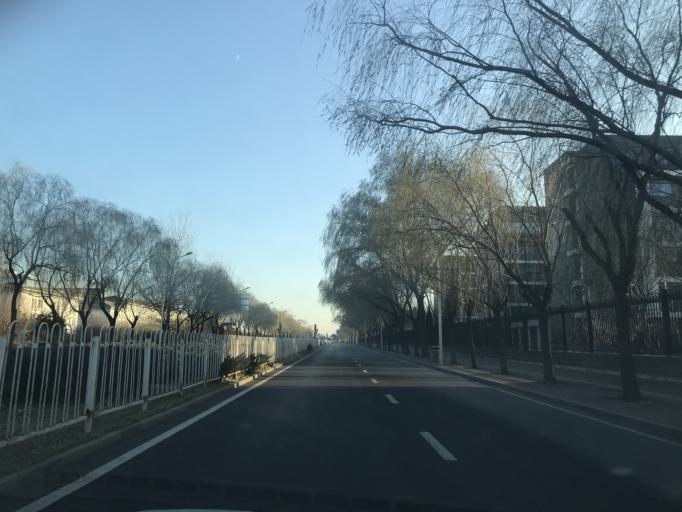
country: CN
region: Beijing
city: Xibeiwang
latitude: 40.0722
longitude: 116.2495
